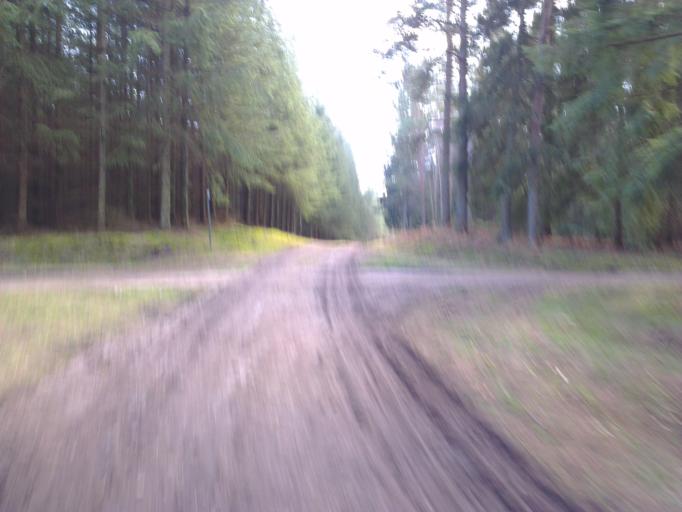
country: DK
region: Capital Region
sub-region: Frederikssund Kommune
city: Jaegerspris
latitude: 55.9185
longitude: 11.9458
